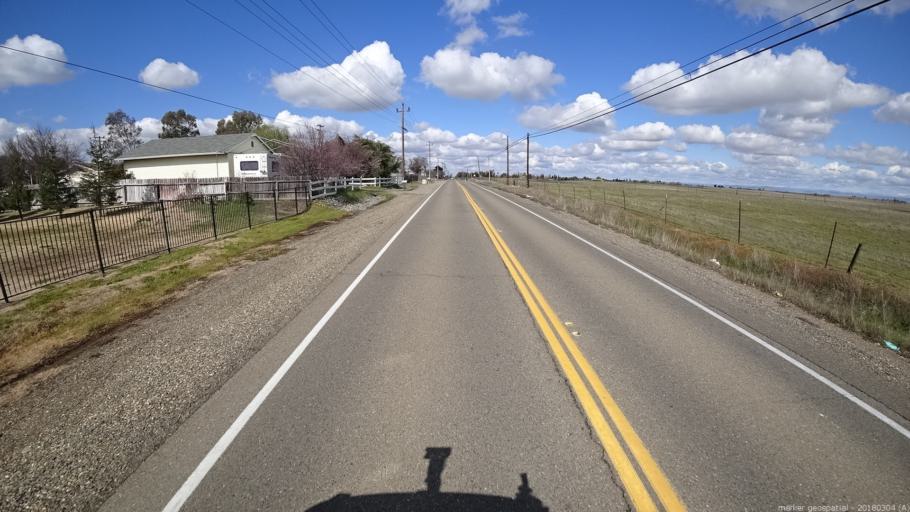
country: US
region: California
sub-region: Sacramento County
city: Vineyard
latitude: 38.4740
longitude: -121.2977
